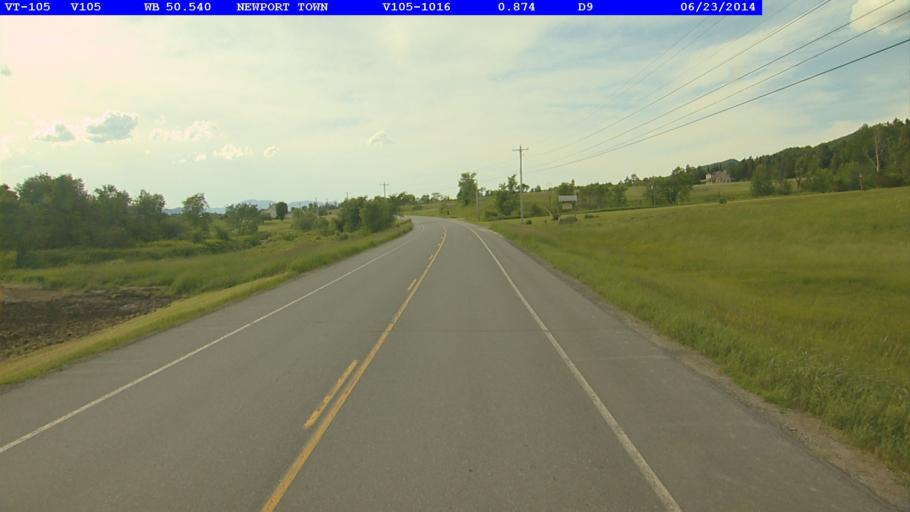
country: US
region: Vermont
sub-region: Orleans County
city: Newport
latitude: 44.9724
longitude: -72.3204
